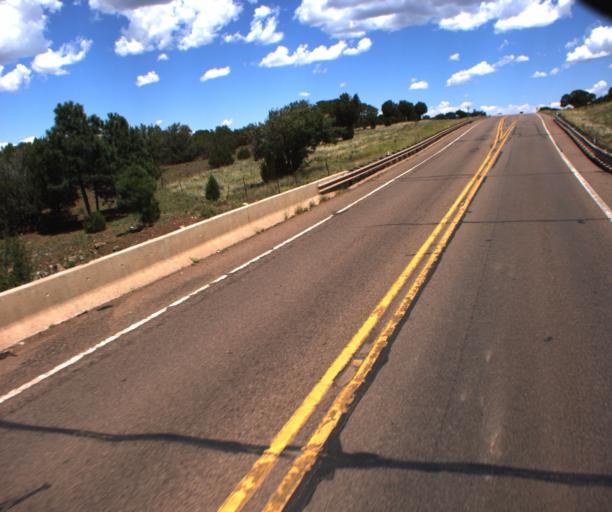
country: US
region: Arizona
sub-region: Navajo County
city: Show Low
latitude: 34.2684
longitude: -109.9373
